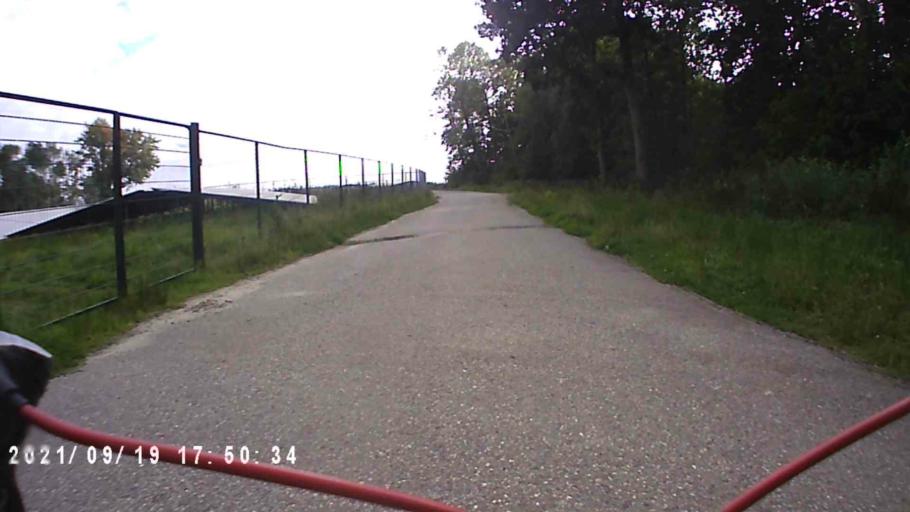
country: NL
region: Groningen
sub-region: Gemeente Delfzijl
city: Delfzijl
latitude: 53.2571
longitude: 6.9449
